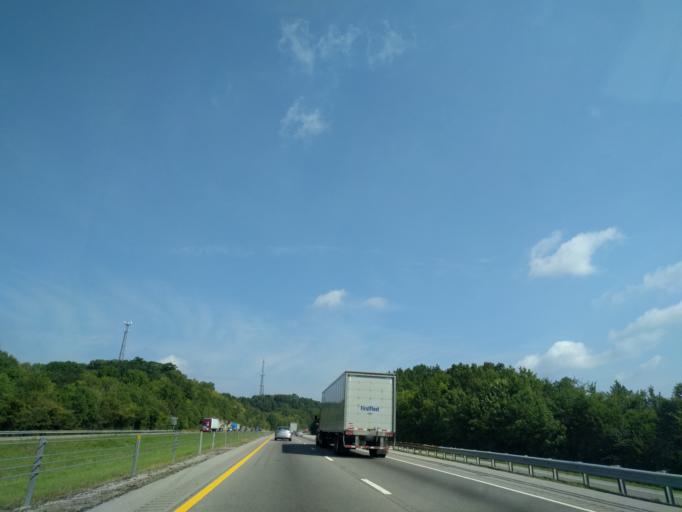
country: US
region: Tennessee
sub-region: Sumner County
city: Millersville
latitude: 36.3505
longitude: -86.7181
